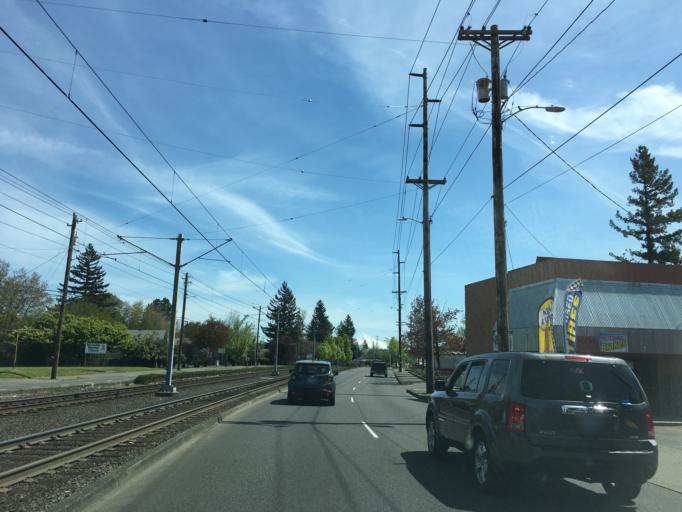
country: US
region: Oregon
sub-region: Multnomah County
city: Fairview
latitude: 45.5219
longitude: -122.4757
